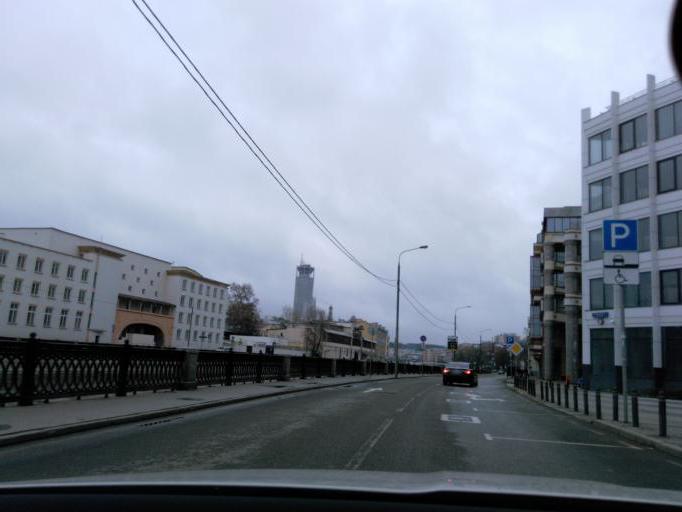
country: RU
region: Moscow
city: Zamoskvorech'ye
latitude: 55.7404
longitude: 37.6381
